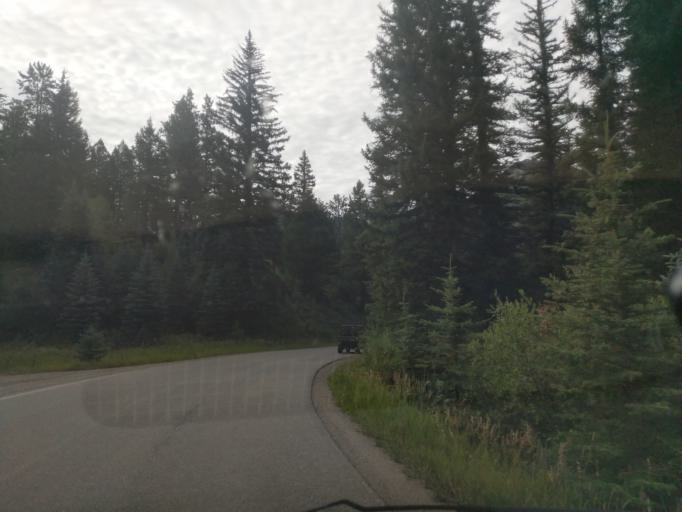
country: US
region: Colorado
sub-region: Gunnison County
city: Crested Butte
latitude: 39.0781
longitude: -107.2254
